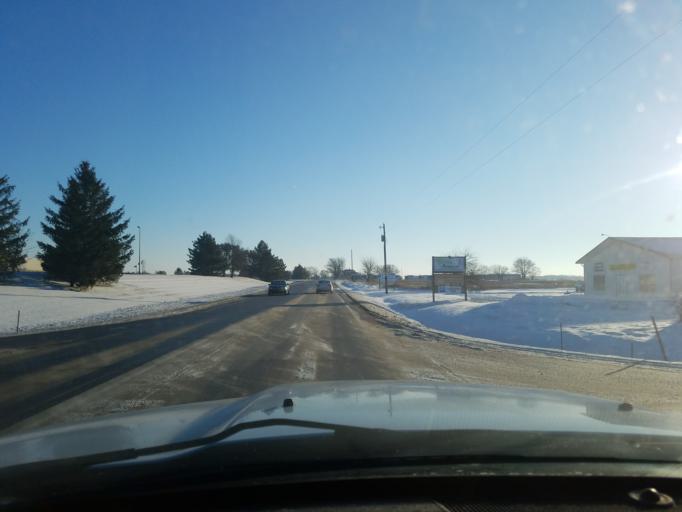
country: US
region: Indiana
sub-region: Noble County
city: Ligonier
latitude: 41.4519
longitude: -85.6057
